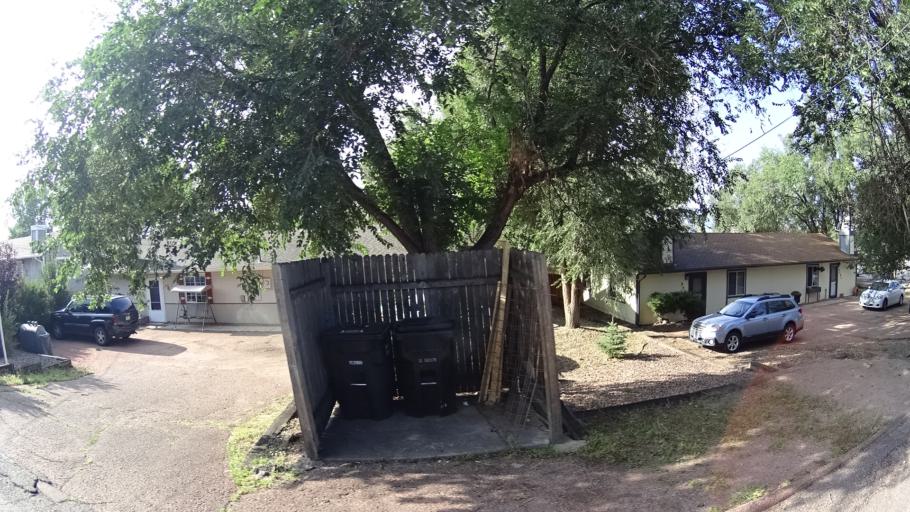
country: US
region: Colorado
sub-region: El Paso County
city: Colorado Springs
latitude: 38.8847
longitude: -104.8030
